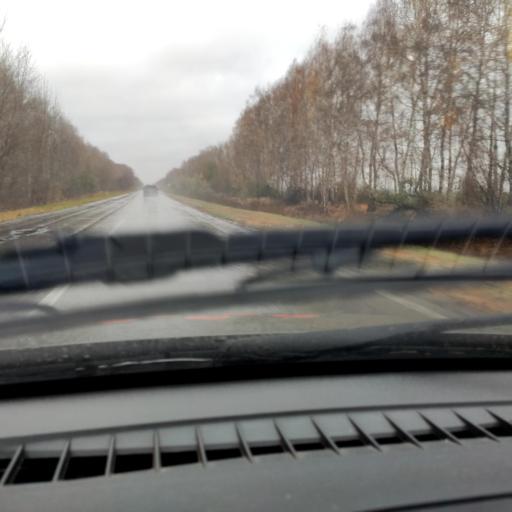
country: RU
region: Samara
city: Tol'yatti
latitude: 53.6701
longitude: 49.2740
